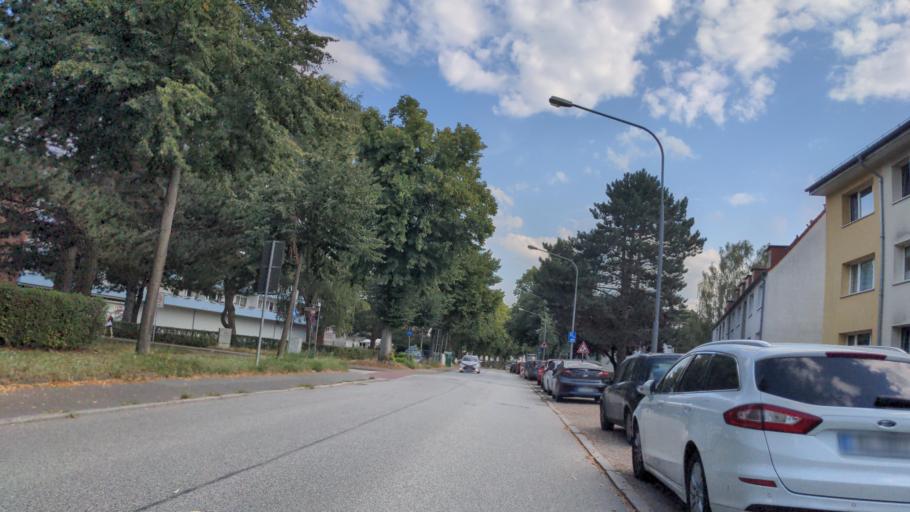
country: DE
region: Schleswig-Holstein
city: Luebeck
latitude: 53.8730
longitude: 10.7191
